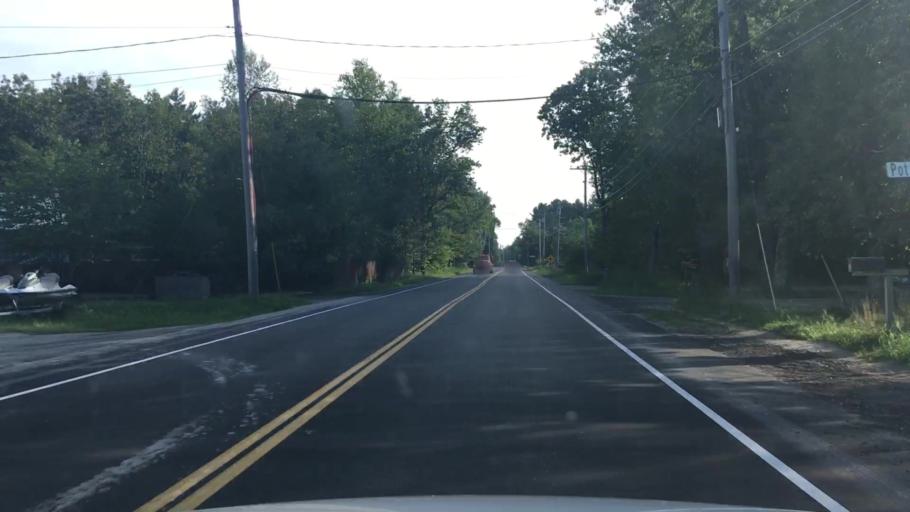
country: US
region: Maine
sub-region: Cumberland County
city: North Windham
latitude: 43.8237
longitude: -70.4378
